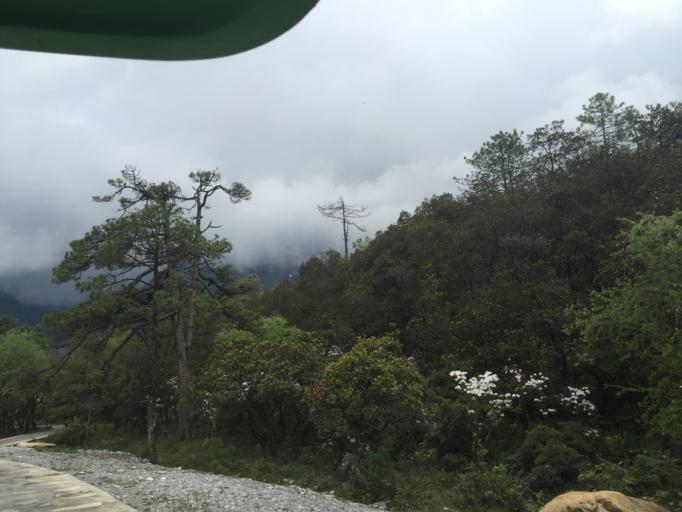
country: CN
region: Yunnan
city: Xiaqiaotou
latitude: 27.1295
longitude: 100.2368
